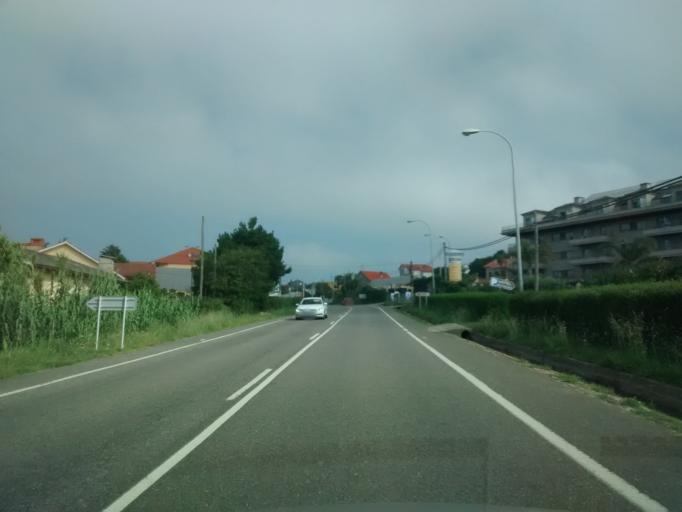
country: ES
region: Galicia
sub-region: Provincia de Pontevedra
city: Sanxenxo
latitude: 42.4020
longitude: -8.8490
